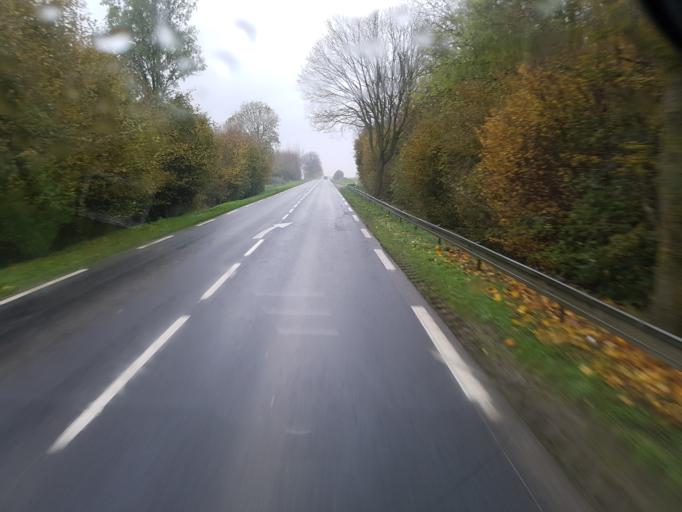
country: FR
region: Picardie
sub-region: Departement de l'Aisne
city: Saint-Quentin
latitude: 49.8843
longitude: 3.2668
